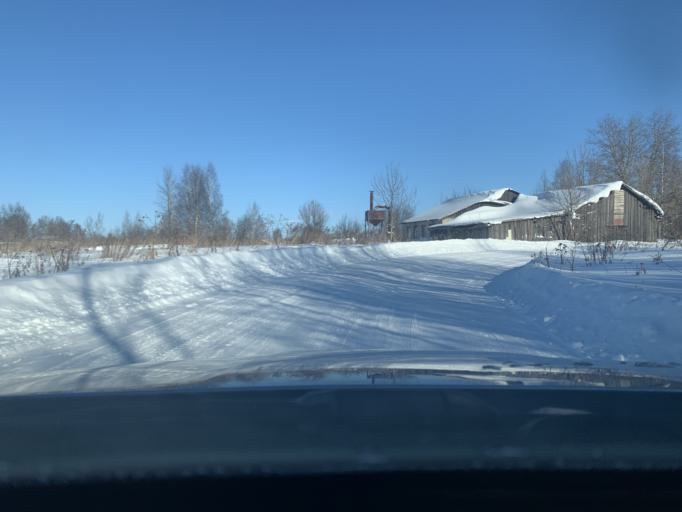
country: RU
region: Jaroslavl
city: Tunoshna
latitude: 57.6550
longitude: 40.0681
